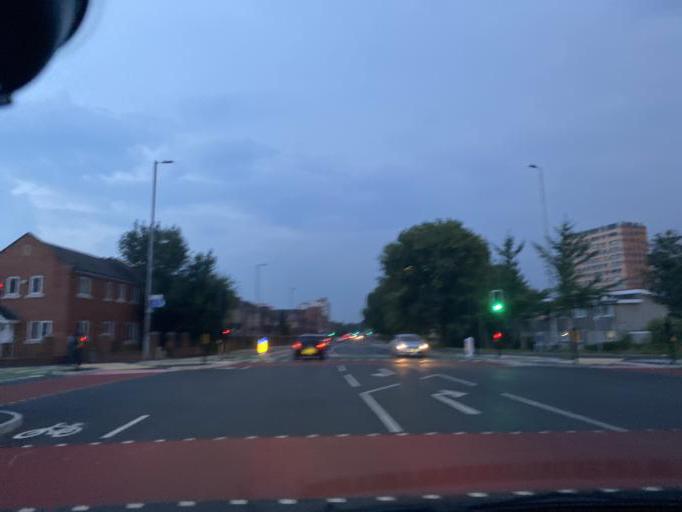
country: GB
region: England
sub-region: Manchester
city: Hulme
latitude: 53.4679
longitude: -2.2576
